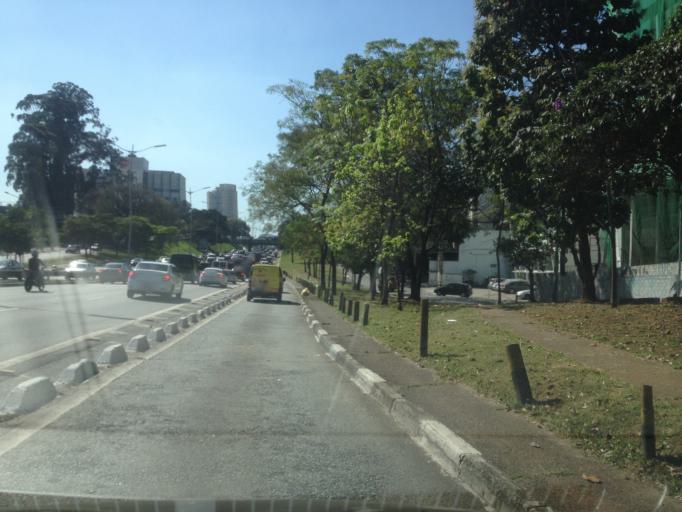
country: BR
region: Sao Paulo
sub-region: Sao Paulo
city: Sao Paulo
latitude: -23.6001
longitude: -46.6509
